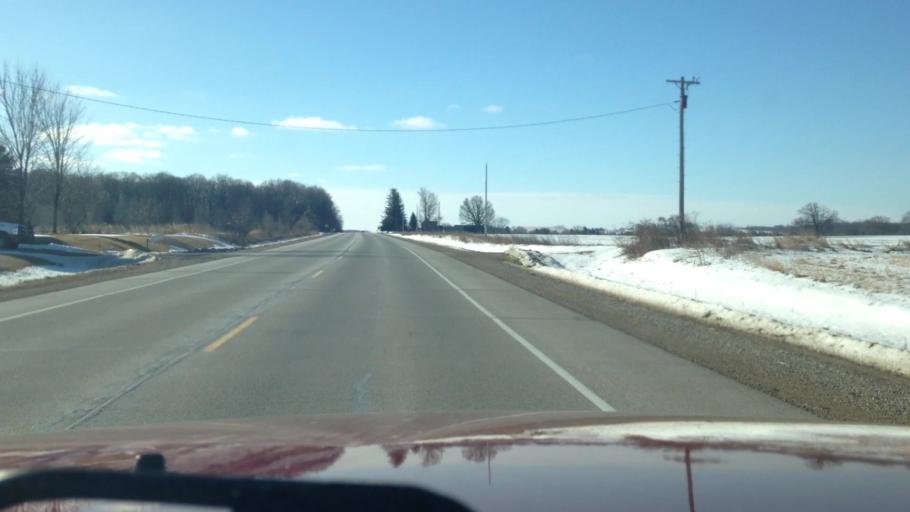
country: US
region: Wisconsin
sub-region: Waukesha County
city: Oconomowoc
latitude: 43.1908
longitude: -88.5080
